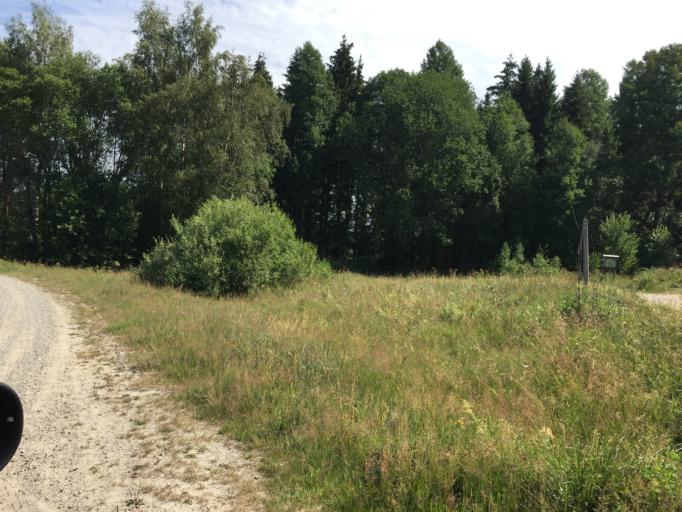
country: SE
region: Stockholm
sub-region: Botkyrka Kommun
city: Tumba
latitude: 59.1567
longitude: 17.8539
